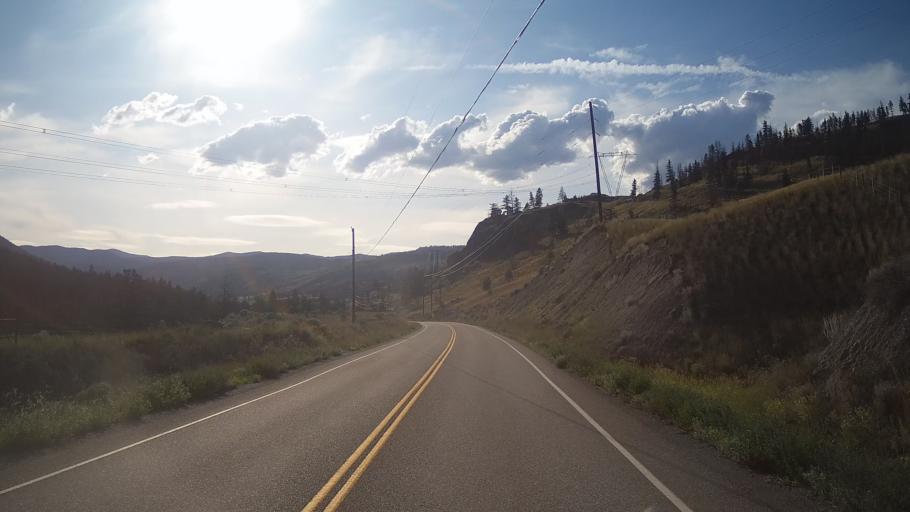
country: CA
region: British Columbia
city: Cache Creek
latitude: 50.8853
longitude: -121.4316
